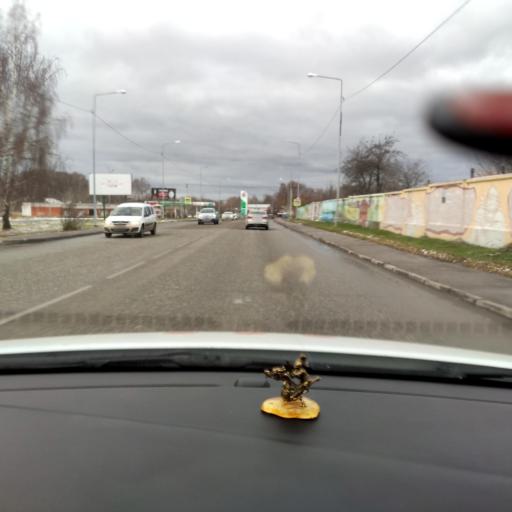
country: RU
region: Tatarstan
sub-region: Zelenodol'skiy Rayon
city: Zelenodolsk
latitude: 55.8458
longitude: 48.5525
